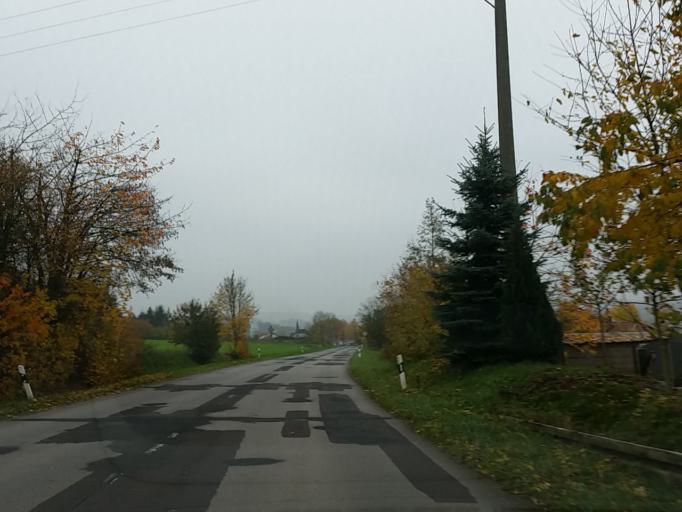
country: DE
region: Saarland
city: Lebach
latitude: 49.4189
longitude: 6.9050
